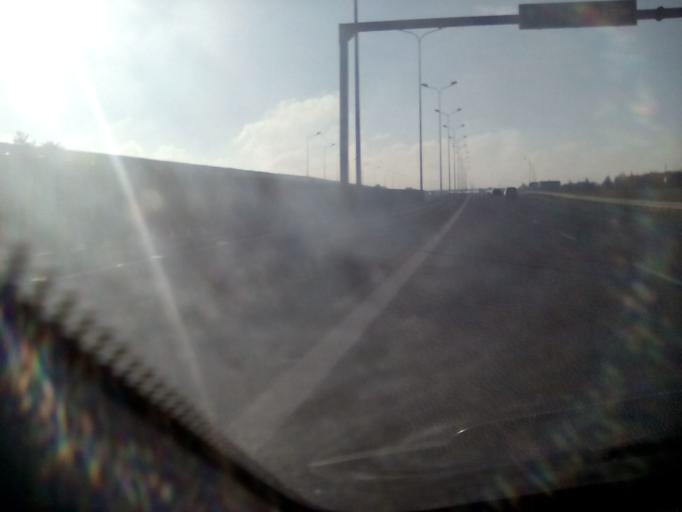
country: PL
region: Masovian Voivodeship
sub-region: Powiat grojecki
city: Grojec
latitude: 51.8376
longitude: 20.8762
